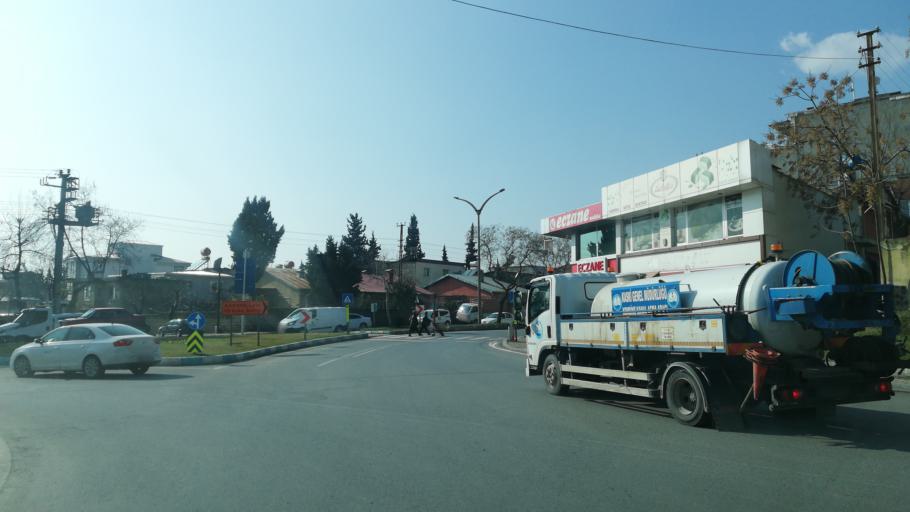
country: TR
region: Kahramanmaras
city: Kahramanmaras
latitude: 37.5670
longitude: 36.9495
